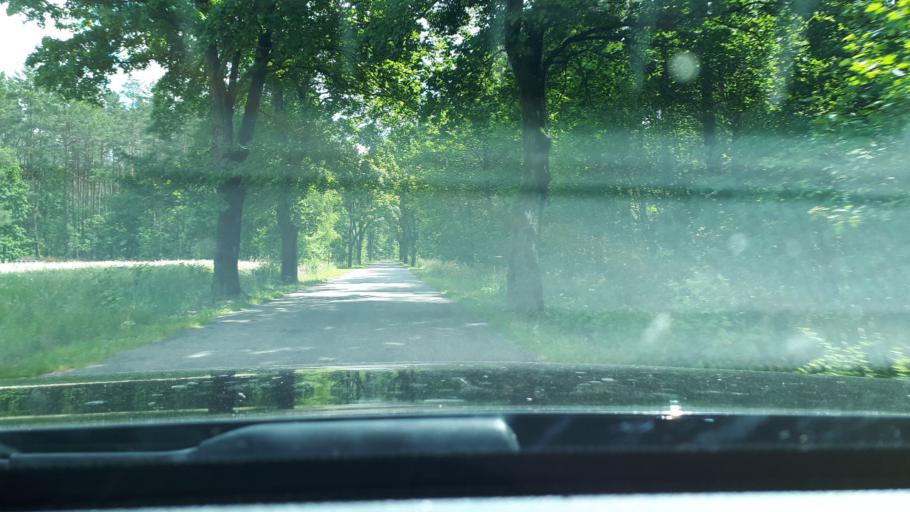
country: PL
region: Warmian-Masurian Voivodeship
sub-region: Powiat olsztynski
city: Olsztynek
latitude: 53.6097
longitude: 20.2565
